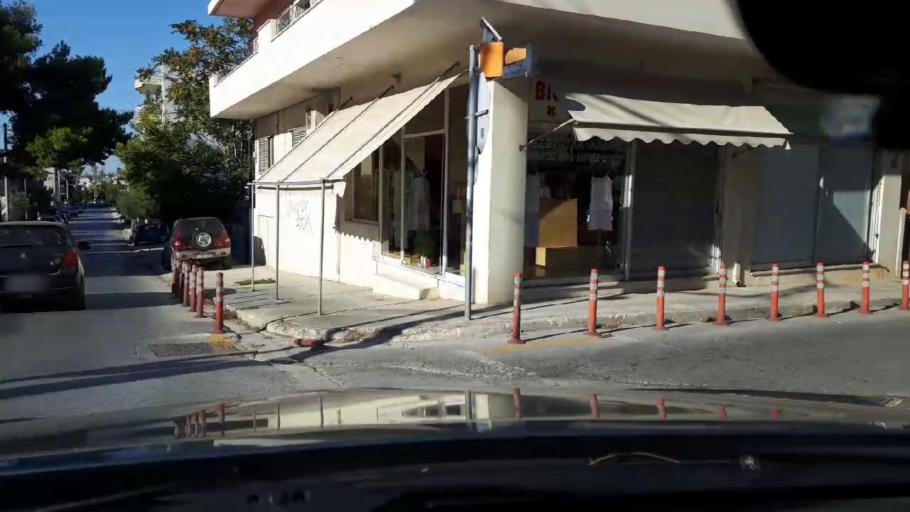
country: GR
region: Attica
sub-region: Nomarchia Anatolikis Attikis
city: Markopoulo
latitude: 37.8834
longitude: 23.9381
